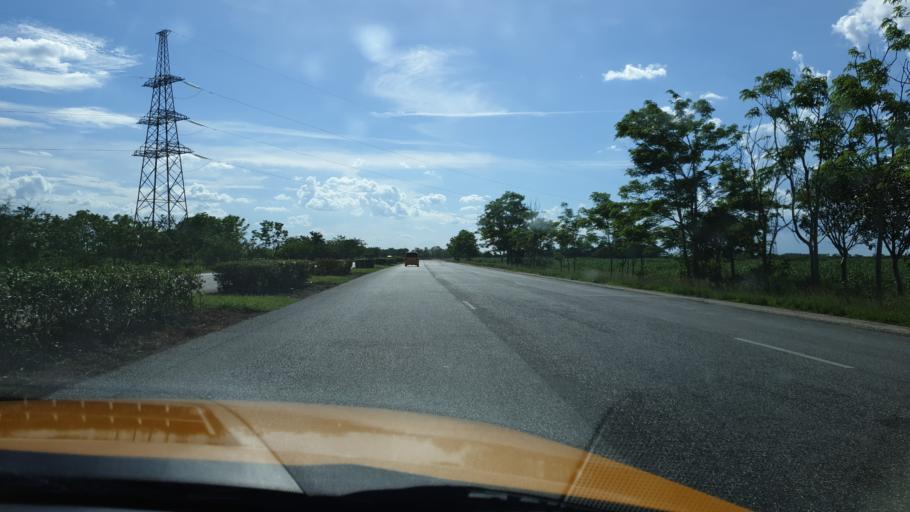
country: CU
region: Cienfuegos
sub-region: Municipio de Aguada de Pasajeros
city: Aguada de Pasajeros
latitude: 22.4088
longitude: -80.8859
